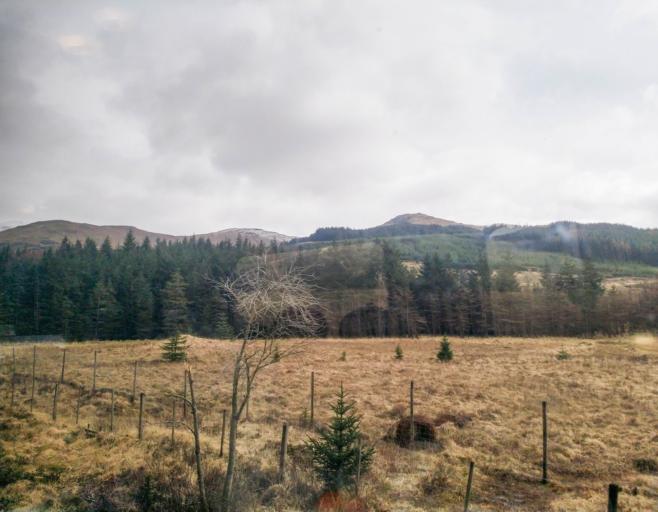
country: GB
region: Scotland
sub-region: Argyll and Bute
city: Garelochhead
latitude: 56.3804
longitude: -4.6340
